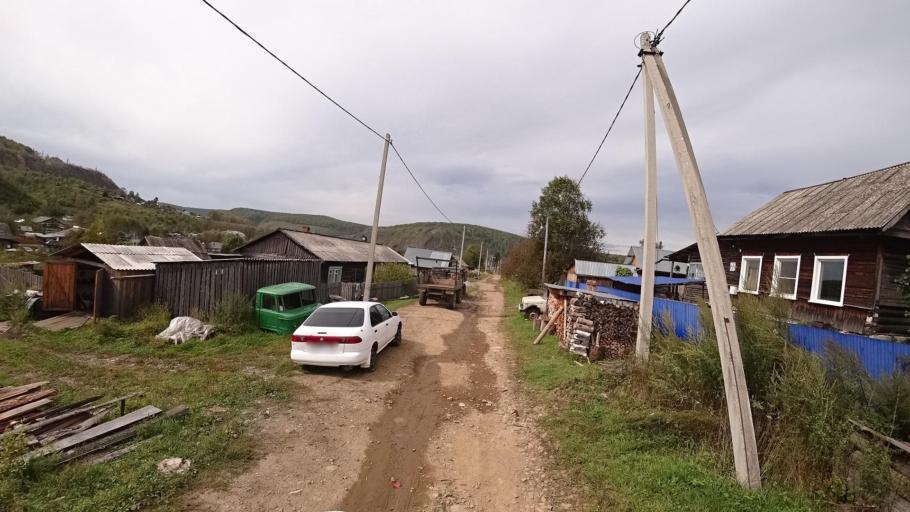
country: RU
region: Jewish Autonomous Oblast
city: Khingansk
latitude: 49.1228
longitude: 131.2074
